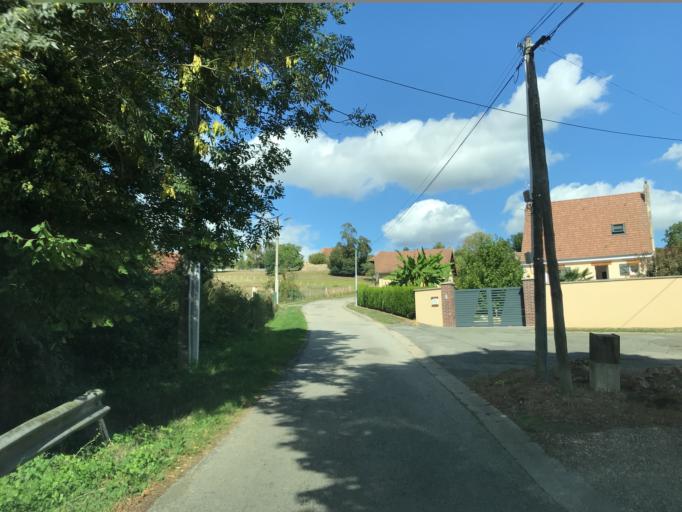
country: FR
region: Haute-Normandie
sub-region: Departement de l'Eure
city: La Chapelle-Reanville
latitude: 49.1125
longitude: 1.3775
